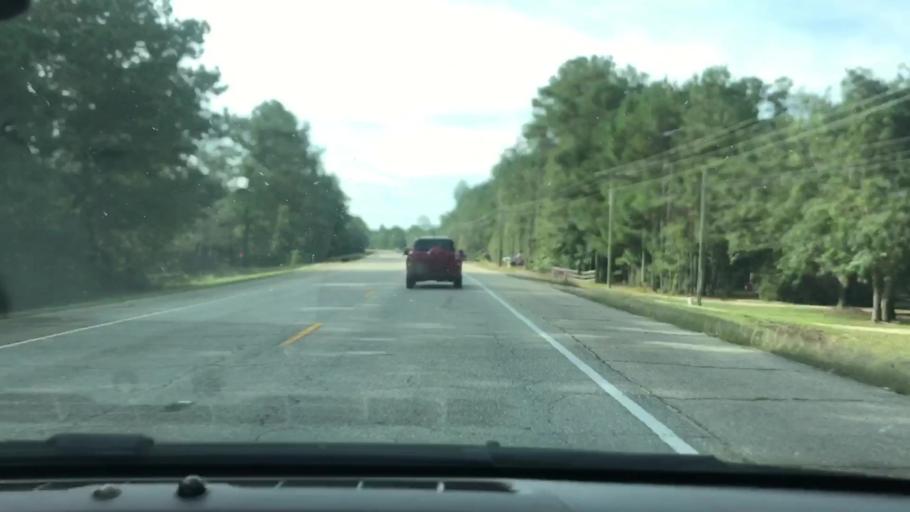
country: US
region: Mississippi
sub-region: Pearl River County
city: Nicholson
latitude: 30.5186
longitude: -89.8370
